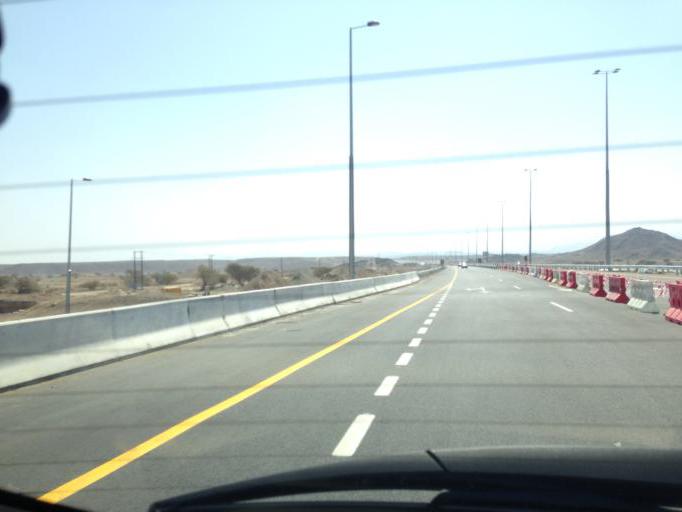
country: OM
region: Al Batinah
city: Rustaq
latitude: 23.5589
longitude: 57.4996
